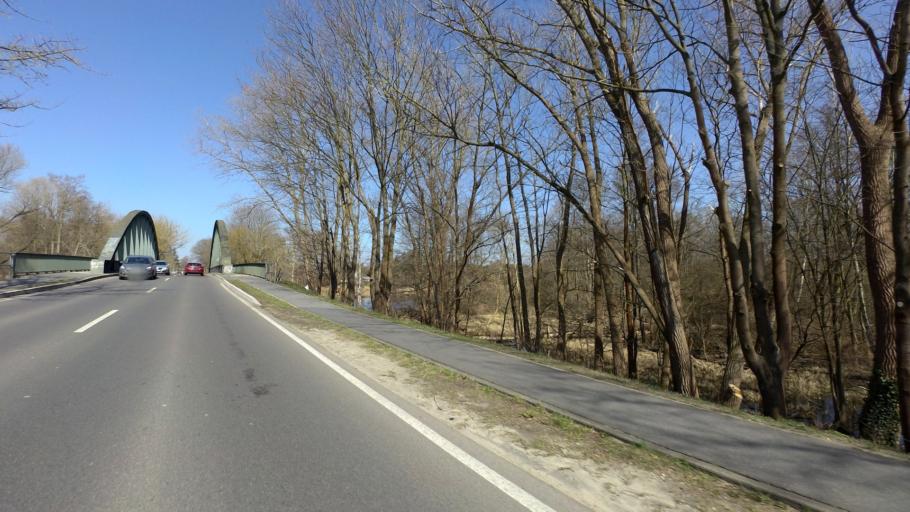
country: DE
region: Brandenburg
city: Oranienburg
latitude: 52.7222
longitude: 13.2511
